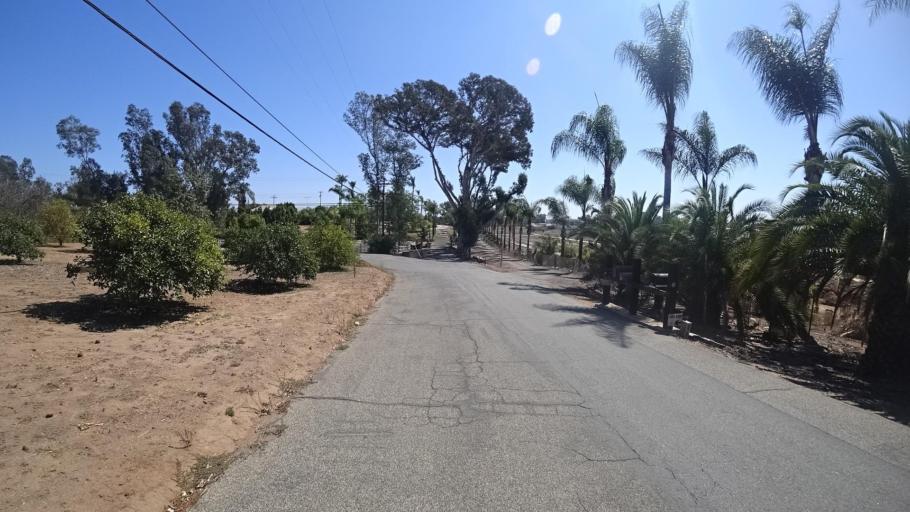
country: US
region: California
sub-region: San Diego County
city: Fallbrook
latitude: 33.3583
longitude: -117.2150
